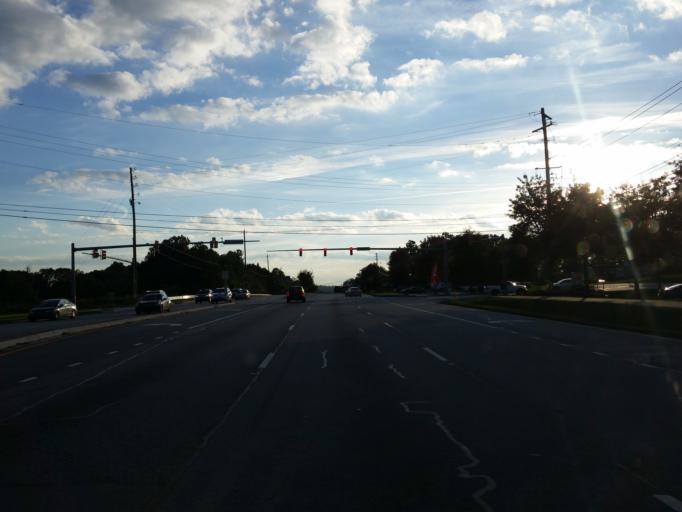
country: US
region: Georgia
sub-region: Cobb County
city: Smyrna
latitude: 33.8421
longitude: -84.5037
